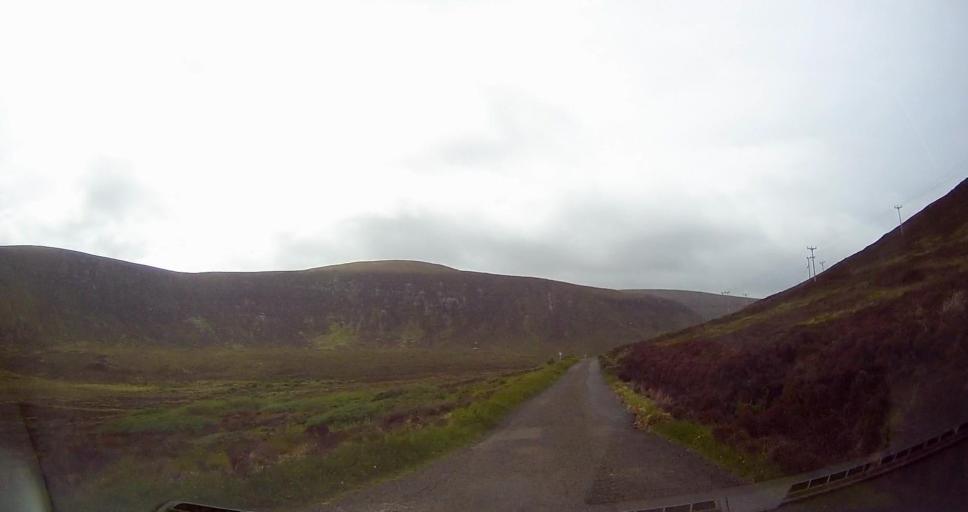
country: GB
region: Scotland
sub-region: Orkney Islands
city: Stromness
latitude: 58.8926
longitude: -3.3145
